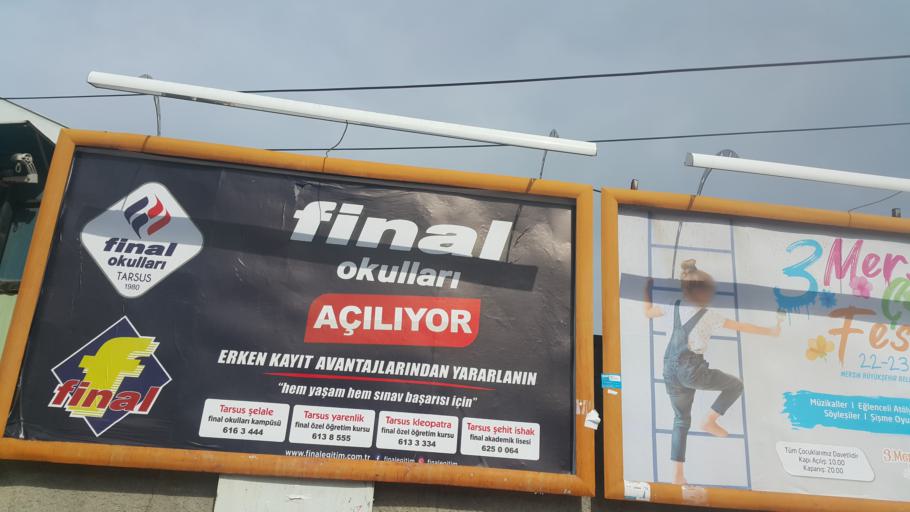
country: TR
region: Mersin
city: Tarsus
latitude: 36.9131
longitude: 34.8924
